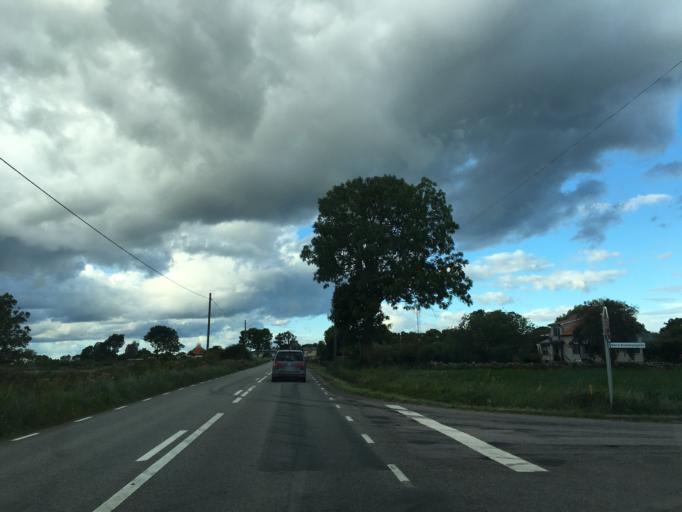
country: SE
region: Kalmar
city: Faerjestaden
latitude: 56.6473
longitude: 16.5167
